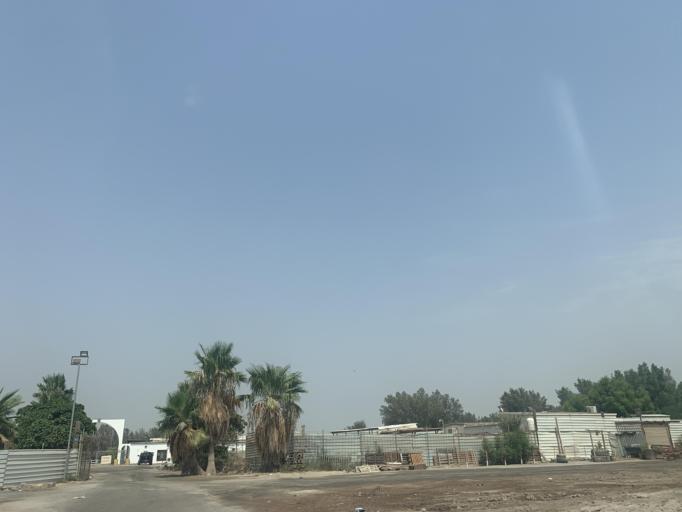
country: BH
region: Manama
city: Jidd Hafs
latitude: 26.2047
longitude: 50.5033
